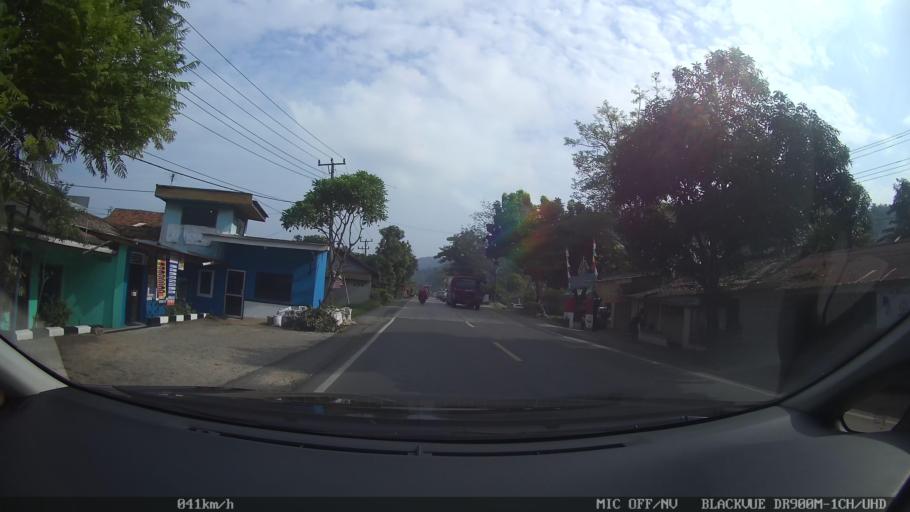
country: ID
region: Lampung
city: Panjang
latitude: -5.4787
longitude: 105.3256
